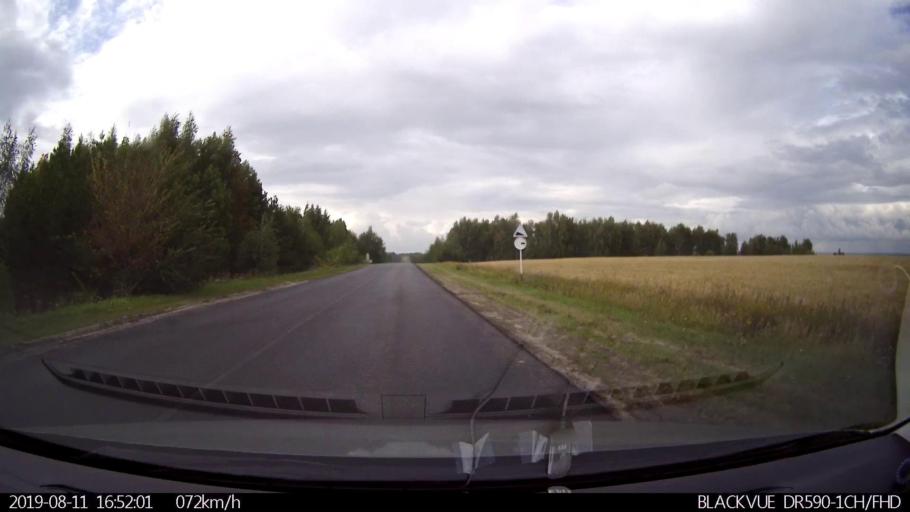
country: RU
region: Ulyanovsk
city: Mayna
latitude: 54.2431
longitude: 47.6754
